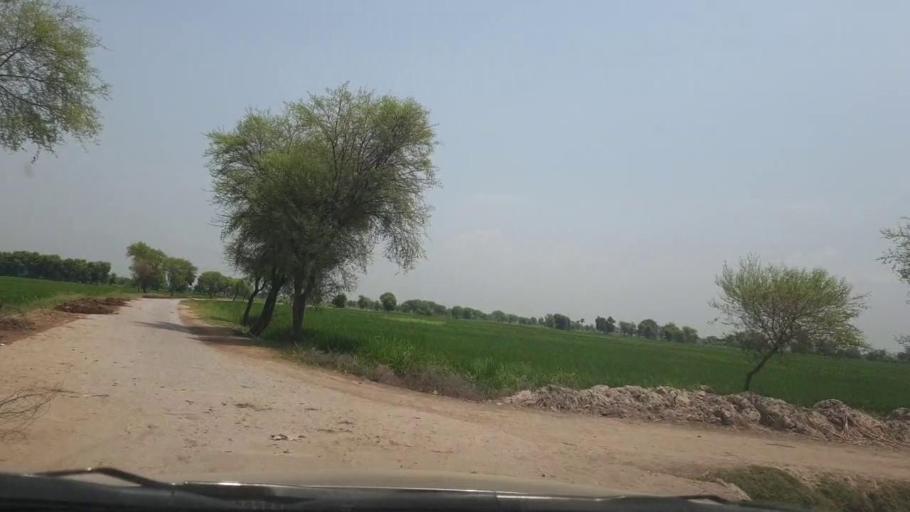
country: PK
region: Sindh
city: Ratodero
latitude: 27.7347
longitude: 68.2994
